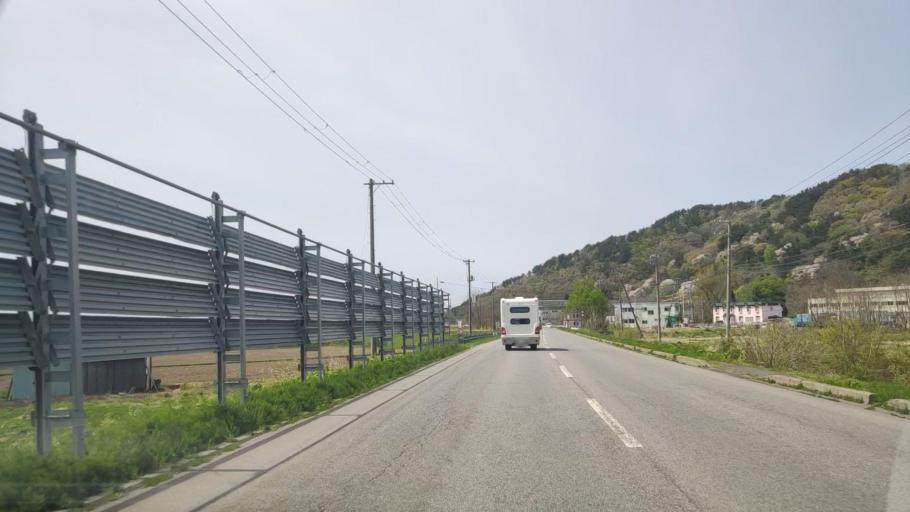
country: JP
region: Aomori
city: Aomori Shi
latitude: 40.8277
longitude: 140.8532
